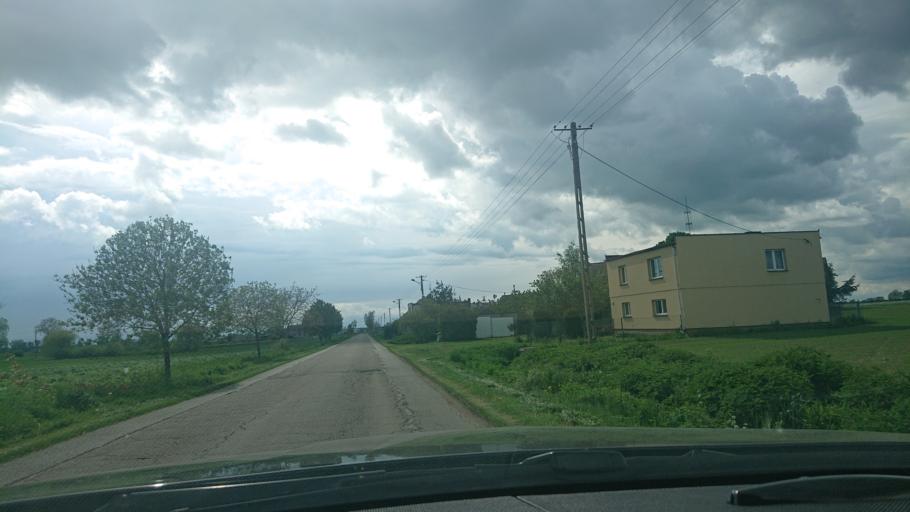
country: PL
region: Greater Poland Voivodeship
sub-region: Powiat gnieznienski
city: Niechanowo
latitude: 52.4775
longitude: 17.6464
